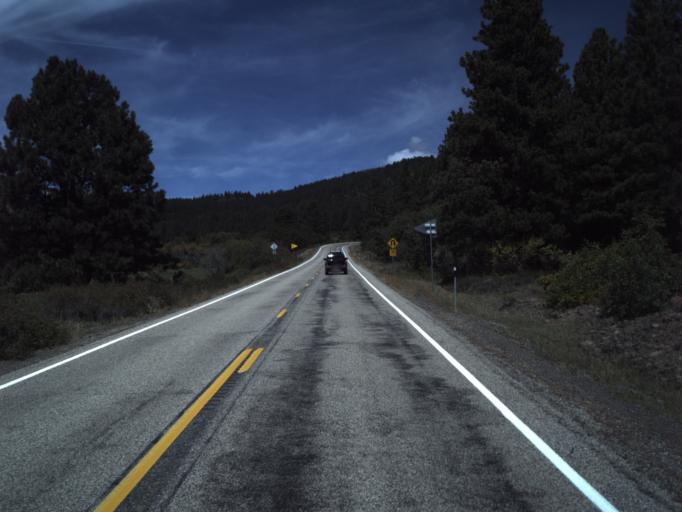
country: US
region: Utah
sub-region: Wayne County
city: Loa
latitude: 37.9912
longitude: -111.4296
